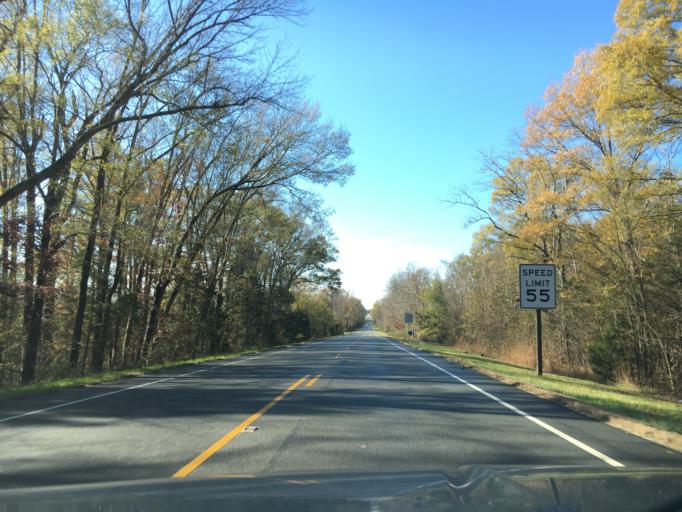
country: US
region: Virginia
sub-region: Cumberland County
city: Cumberland
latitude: 37.5149
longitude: -78.2146
